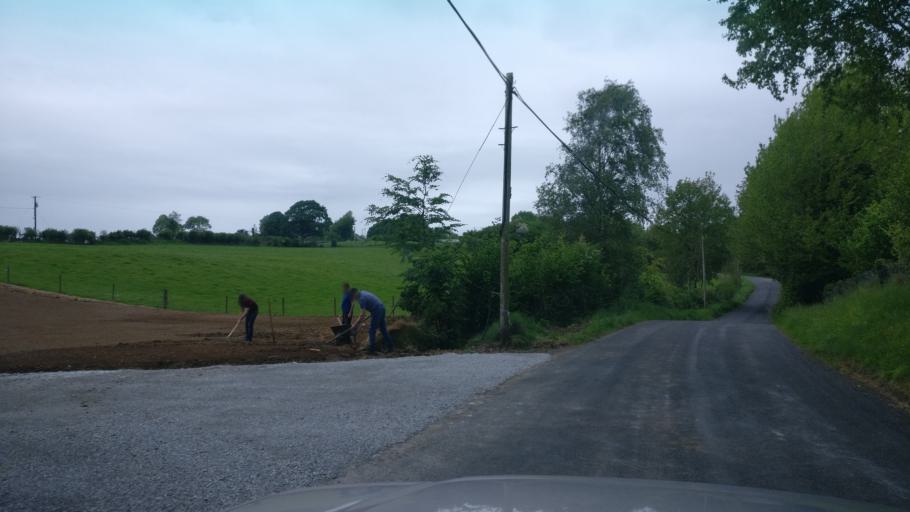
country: IE
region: Connaught
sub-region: County Galway
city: Loughrea
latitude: 53.1105
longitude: -8.4046
